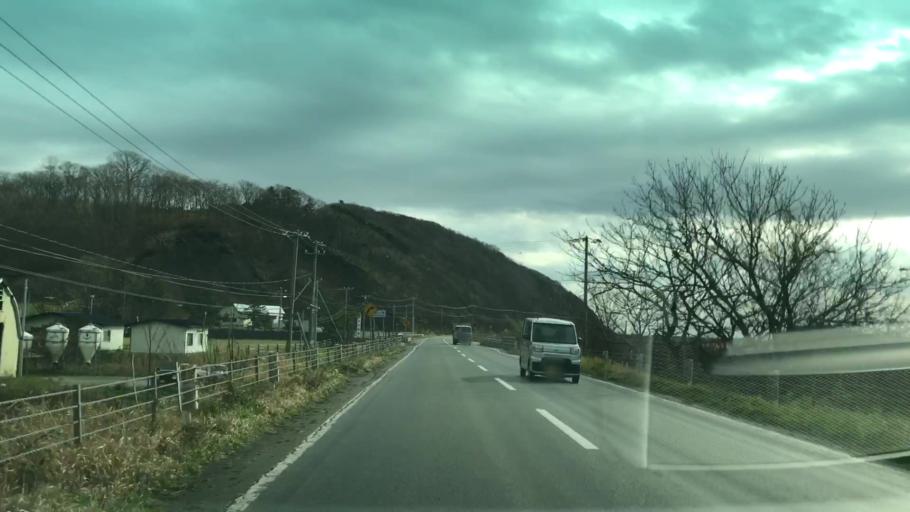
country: JP
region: Hokkaido
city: Shizunai-furukawacho
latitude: 42.1416
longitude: 142.8525
